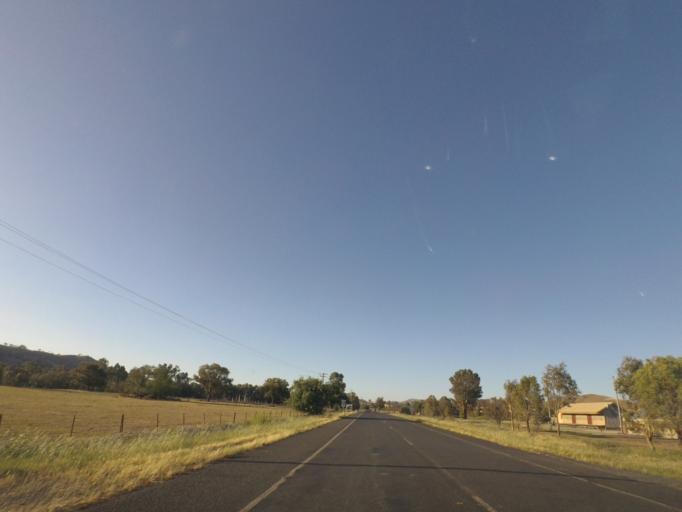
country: AU
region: New South Wales
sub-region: Gundagai
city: Gundagai
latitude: -34.9339
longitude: 148.1670
